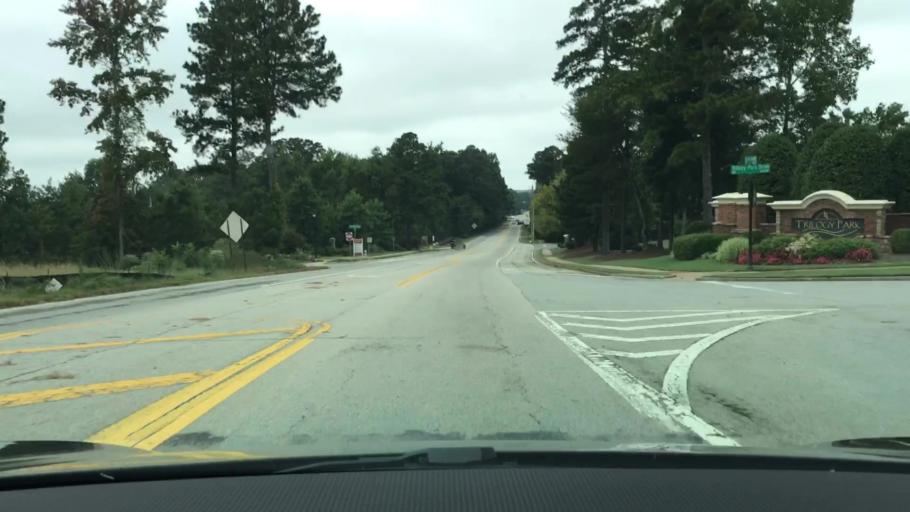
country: US
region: Georgia
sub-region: Barrow County
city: Auburn
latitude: 34.0718
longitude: -83.8494
